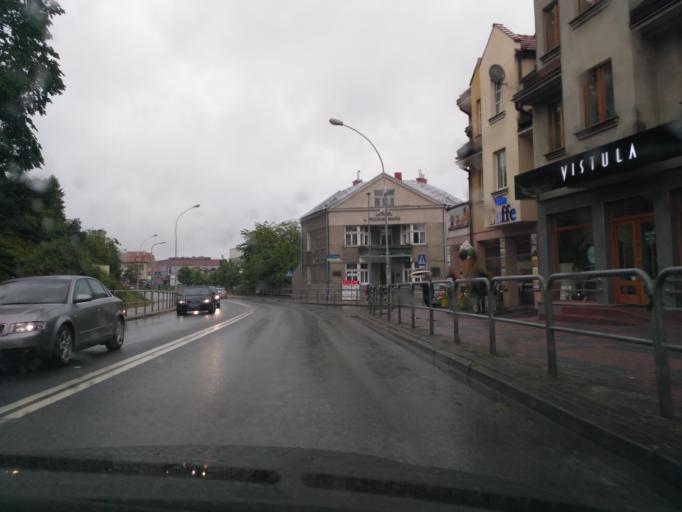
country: PL
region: Lesser Poland Voivodeship
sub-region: Powiat gorlicki
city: Gorlice
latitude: 49.6576
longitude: 21.1595
